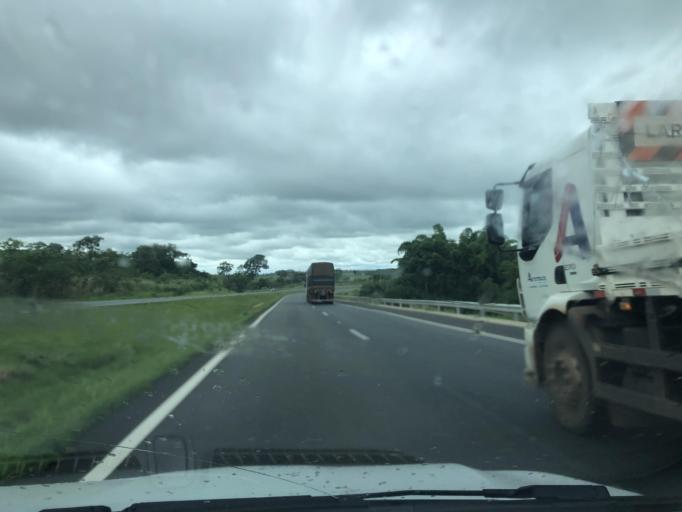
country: BR
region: Goias
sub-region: Catalao
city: Catalao
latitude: -18.2687
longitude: -47.9999
